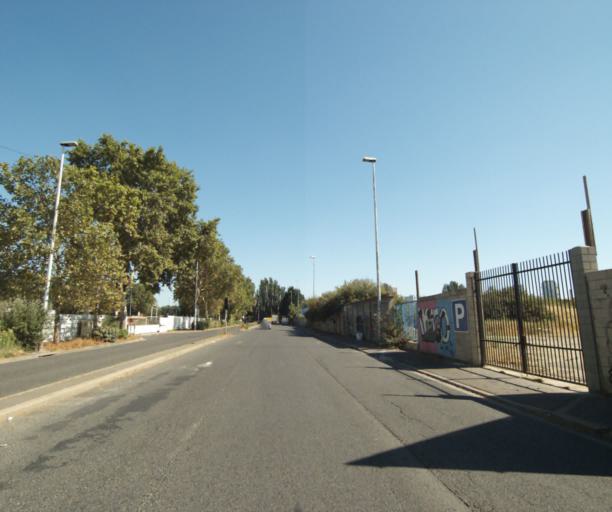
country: FR
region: Ile-de-France
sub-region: Departement des Hauts-de-Seine
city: Villeneuve-la-Garenne
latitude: 48.9244
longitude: 2.3261
